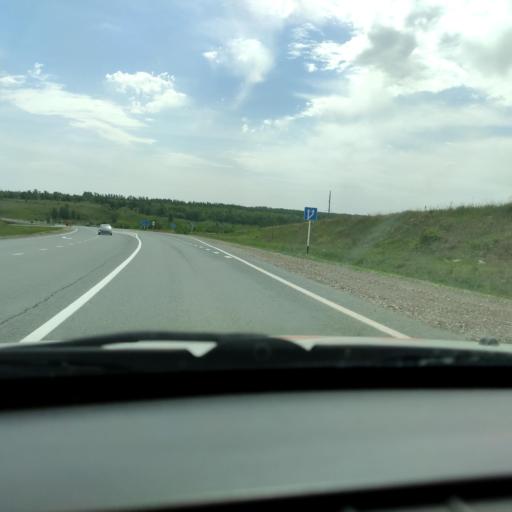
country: RU
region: Samara
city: Bereza
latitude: 53.6505
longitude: 50.2166
